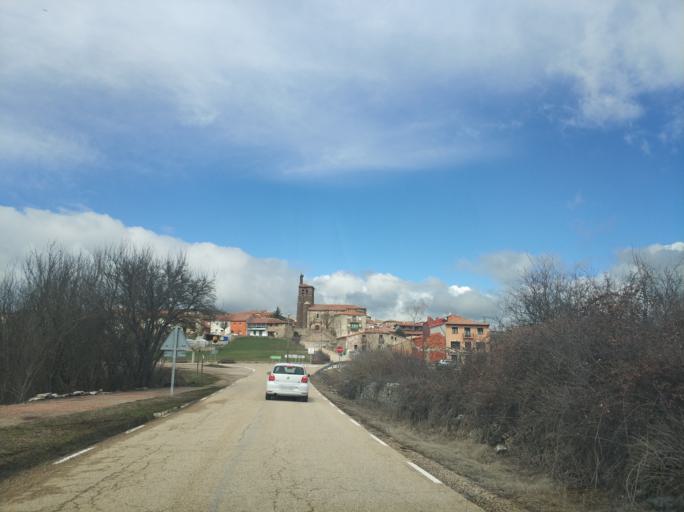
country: ES
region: Castille and Leon
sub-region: Provincia de Soria
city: Abejar
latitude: 41.8058
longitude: -2.7819
